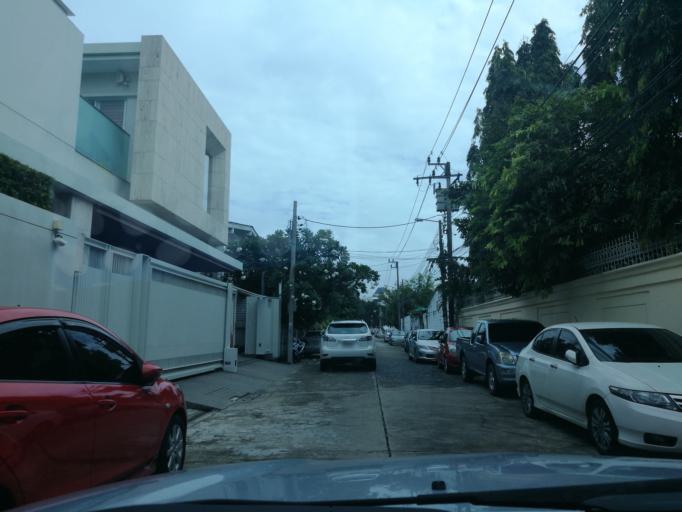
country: TH
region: Bangkok
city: Phaya Thai
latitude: 13.7866
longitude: 100.5411
